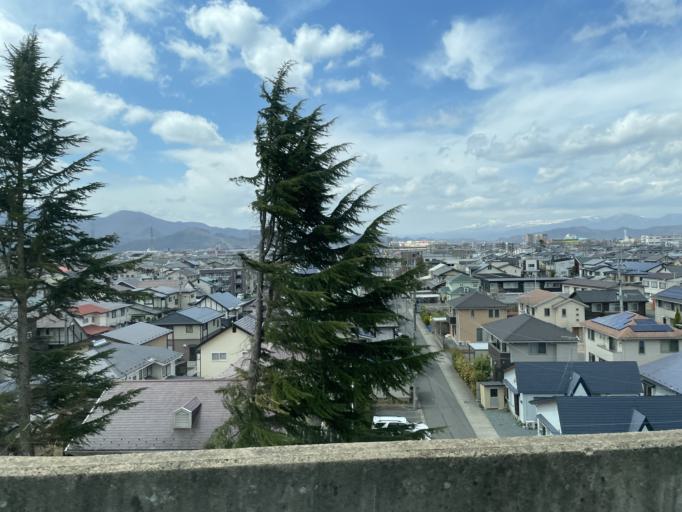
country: JP
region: Iwate
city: Morioka-shi
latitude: 39.6811
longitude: 141.1487
